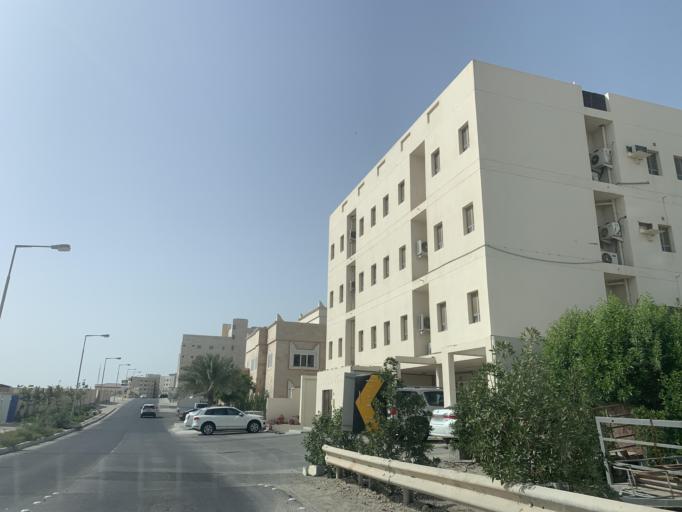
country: BH
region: Northern
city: Ar Rifa'
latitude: 26.1492
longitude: 50.5695
